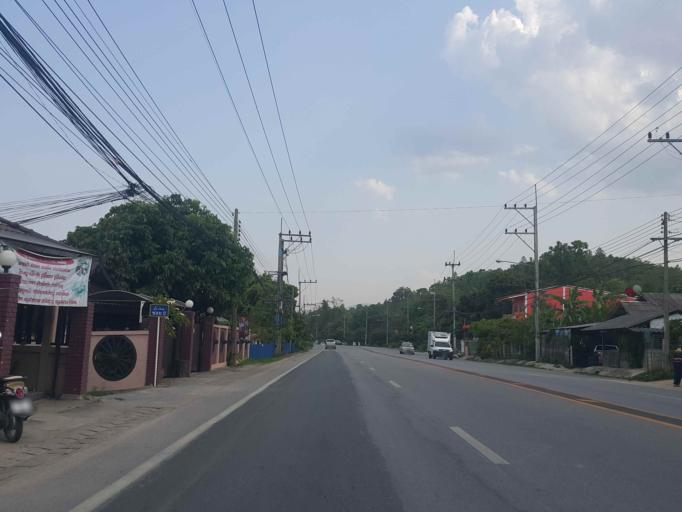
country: TH
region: Chiang Mai
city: Mae Taeng
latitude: 18.9802
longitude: 98.9455
